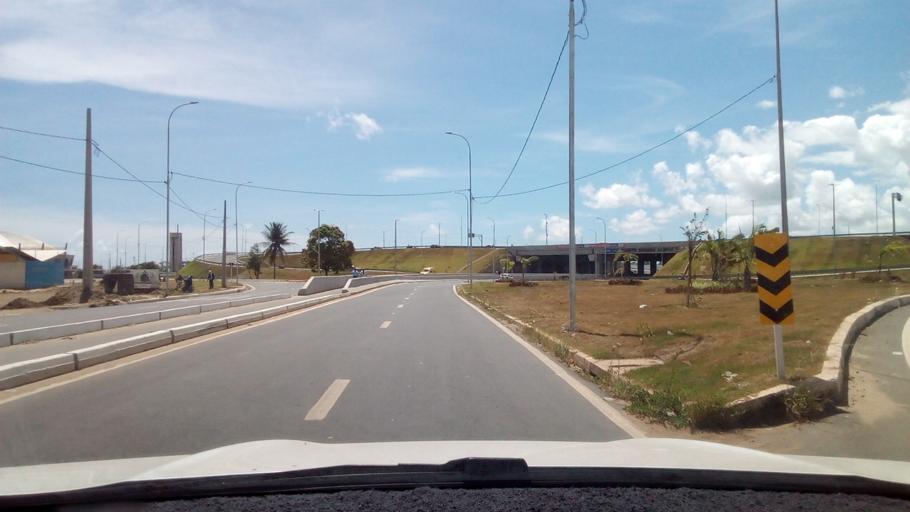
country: BR
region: Paraiba
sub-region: Joao Pessoa
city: Joao Pessoa
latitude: -7.1677
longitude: -34.8751
